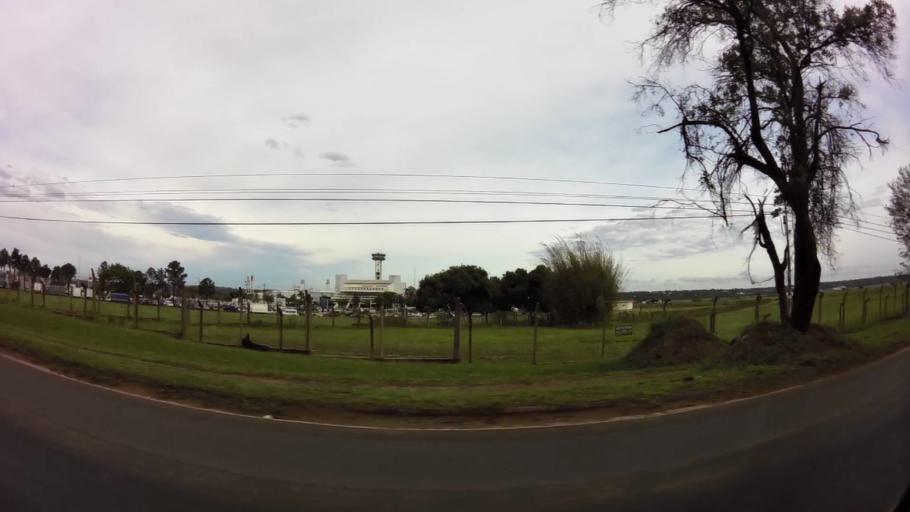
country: PY
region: Central
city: Limpio
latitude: -25.2418
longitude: -57.5106
